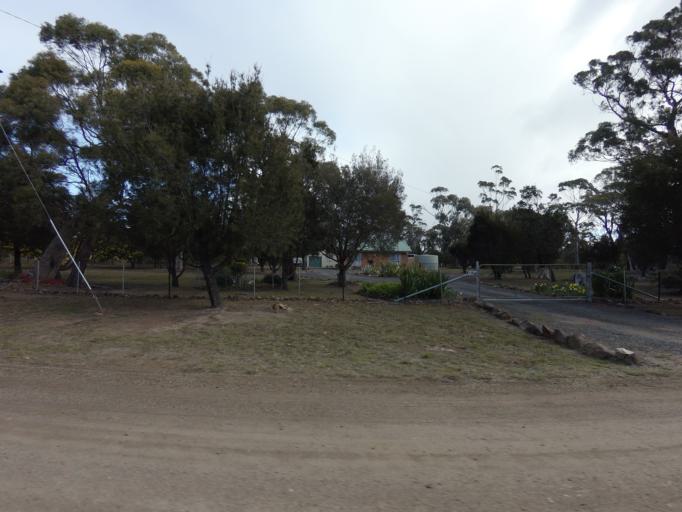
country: AU
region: Tasmania
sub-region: Sorell
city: Sorell
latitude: -42.3264
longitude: 147.9567
